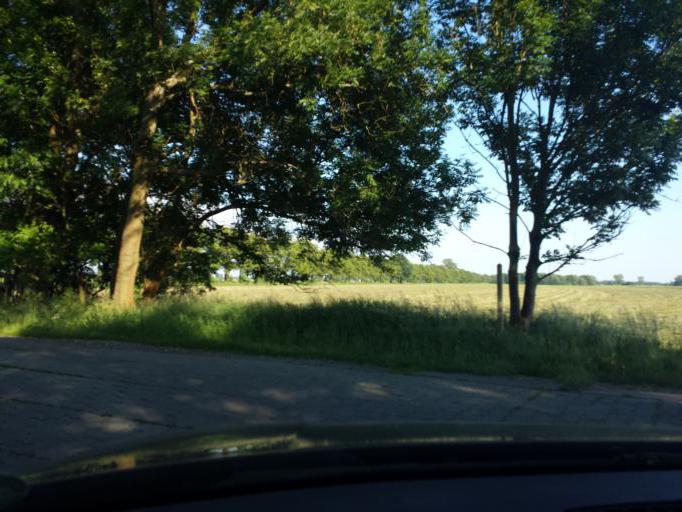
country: DE
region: Brandenburg
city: Ruthnick
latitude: 52.8395
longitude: 12.9295
